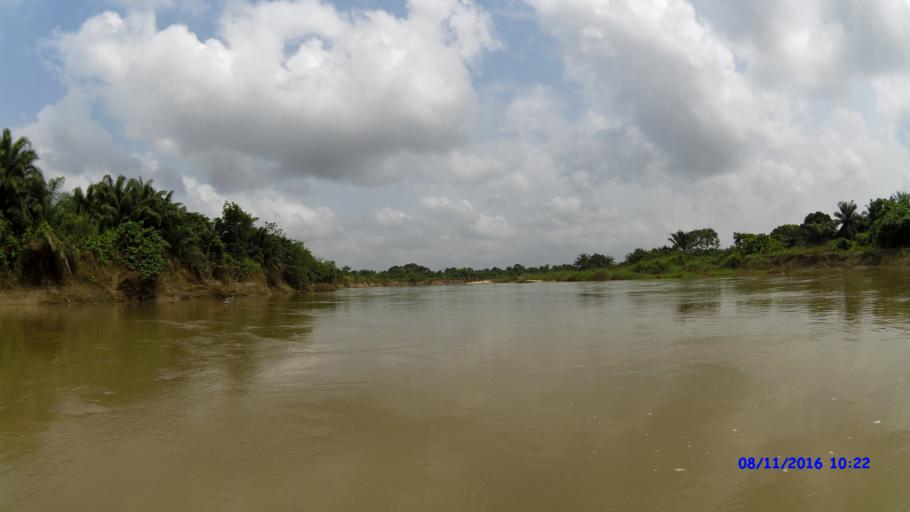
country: BJ
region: Mono
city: Come
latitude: 6.4653
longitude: 1.7475
